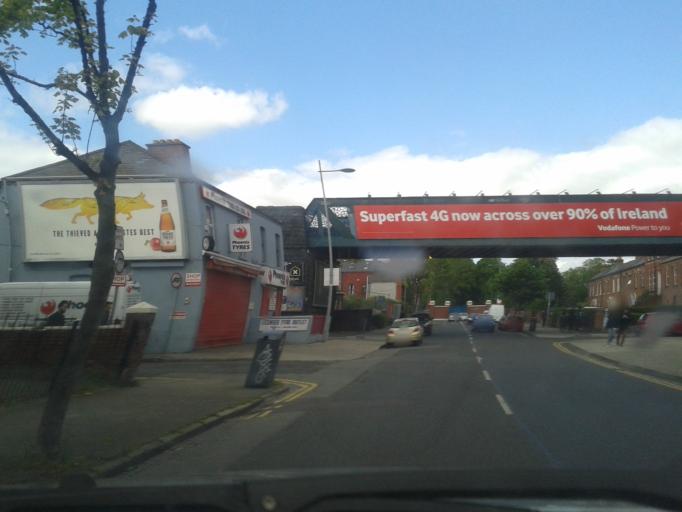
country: IE
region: Leinster
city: Drumcondra
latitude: 53.3615
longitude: -6.2530
